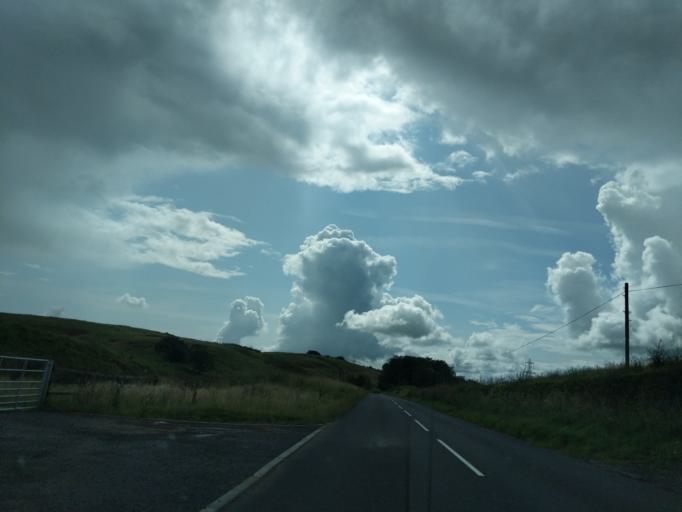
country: GB
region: Scotland
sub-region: East Renfrewshire
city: Neilston
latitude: 55.7451
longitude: -4.4656
